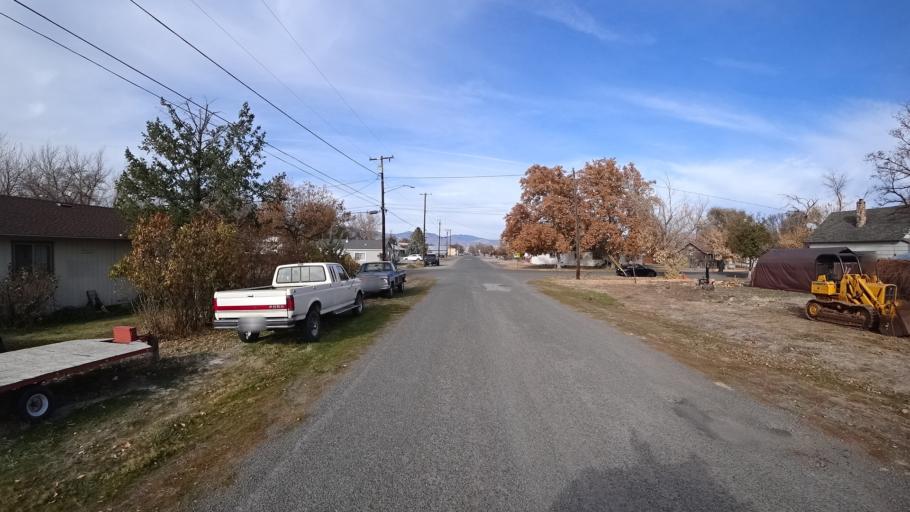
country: US
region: California
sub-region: Siskiyou County
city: Montague
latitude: 41.7257
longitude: -122.5251
